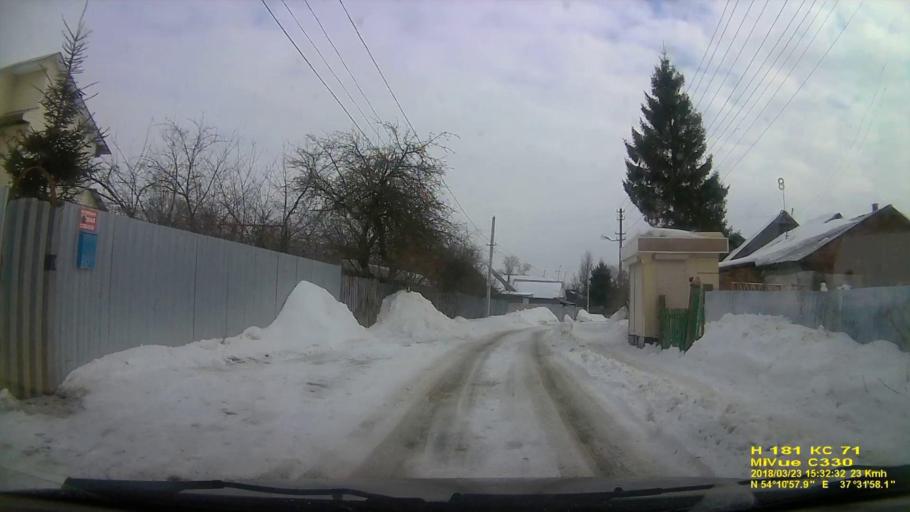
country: RU
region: Tula
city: Kosaya Gora
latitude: 54.1827
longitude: 37.5328
